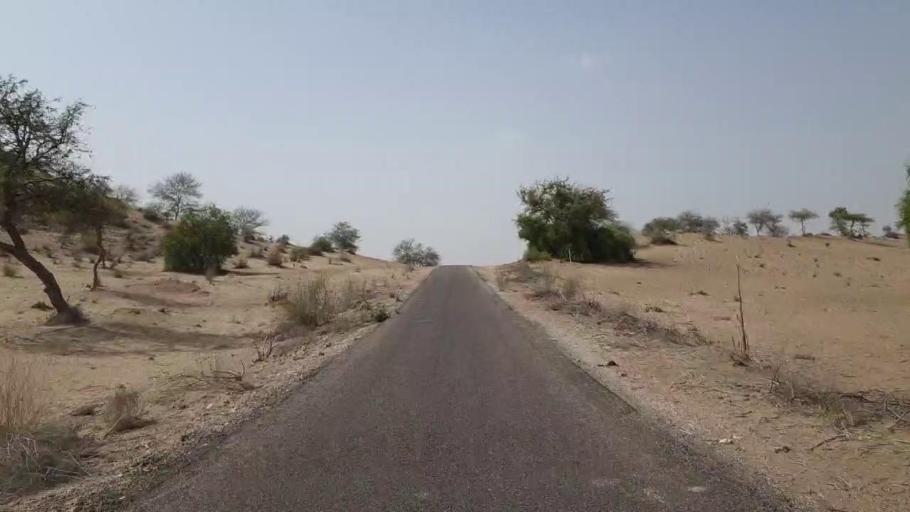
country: PK
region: Sindh
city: Mithi
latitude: 24.5879
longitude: 69.9227
